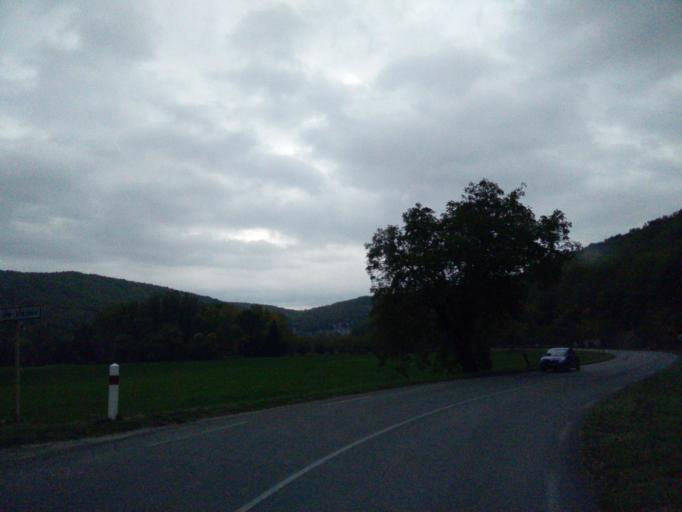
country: FR
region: Midi-Pyrenees
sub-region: Departement du Lot
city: Cahors
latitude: 44.4773
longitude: 1.5483
